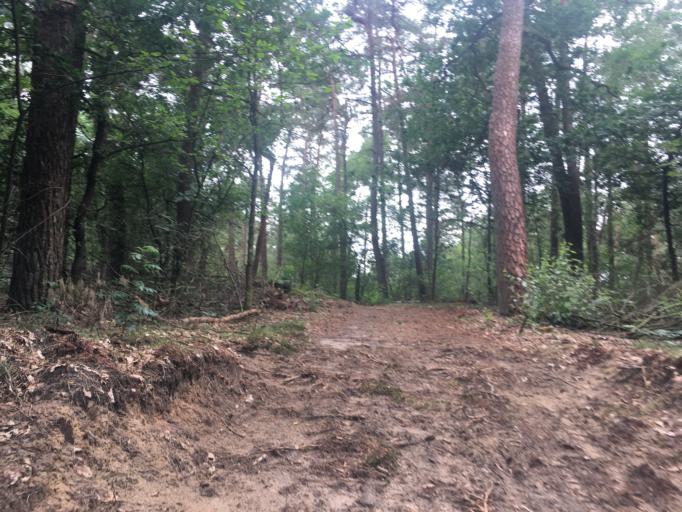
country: NL
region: Drenthe
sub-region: Gemeente Westerveld
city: Dwingeloo
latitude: 52.8857
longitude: 6.3120
